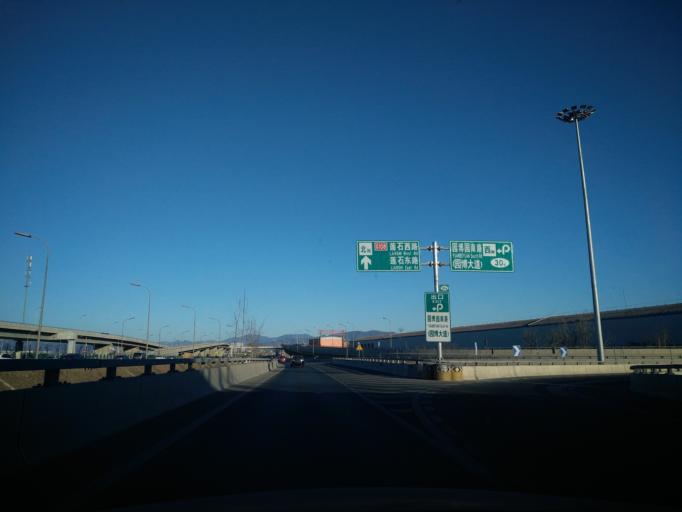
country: CN
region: Beijing
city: Lugu
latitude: 39.8642
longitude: 116.2086
